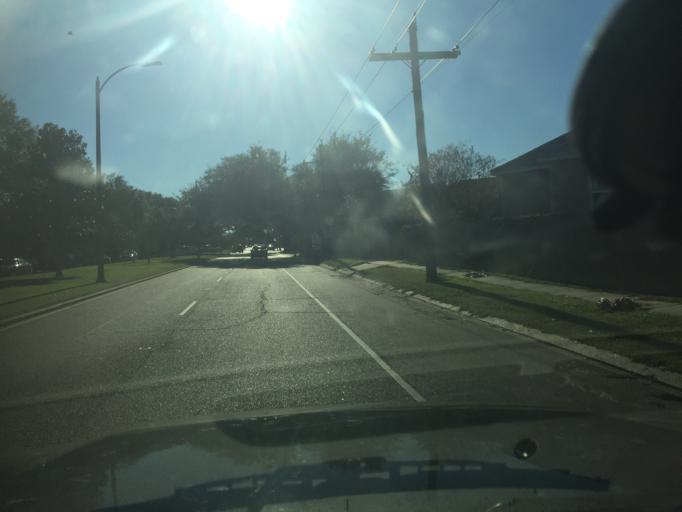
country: US
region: Louisiana
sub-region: Orleans Parish
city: New Orleans
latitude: 29.9859
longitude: -90.0695
